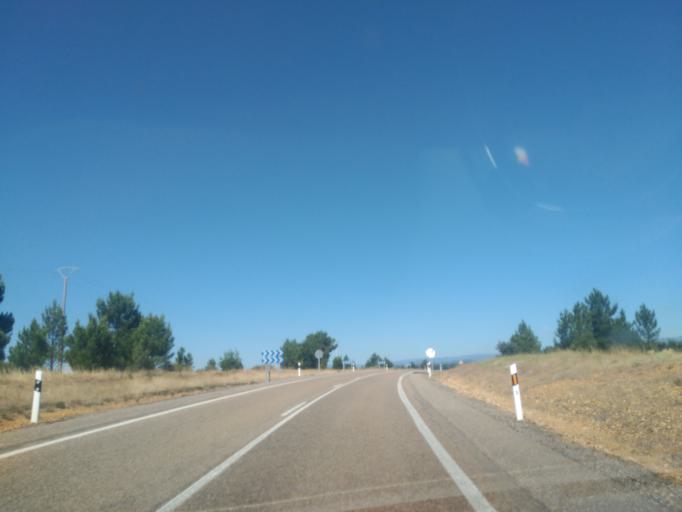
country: ES
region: Castille and Leon
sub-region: Provincia de Zamora
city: Otero de Bodas
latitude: 41.9443
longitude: -6.1885
